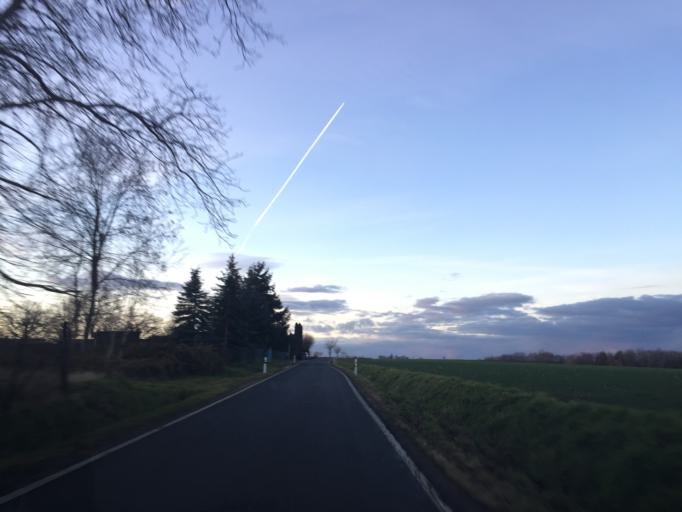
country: DE
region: Thuringia
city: Schmolln
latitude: 50.8986
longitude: 12.3427
